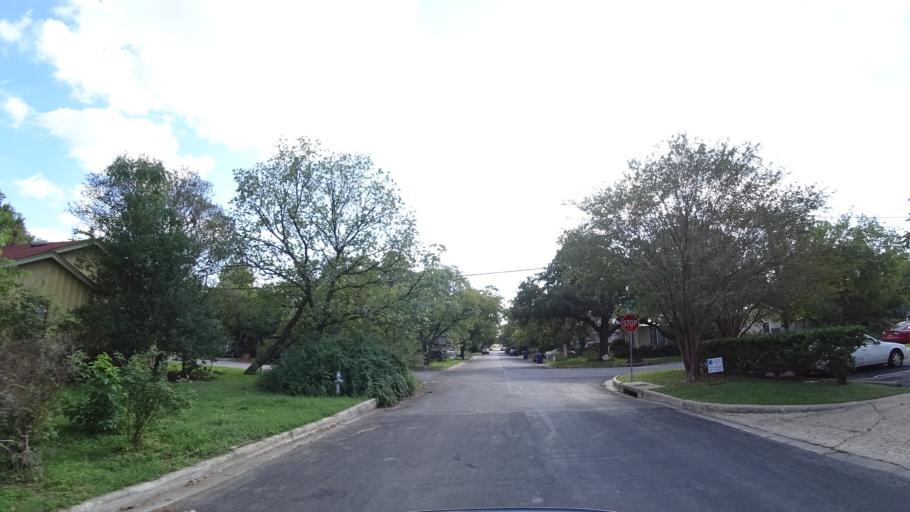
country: US
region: Texas
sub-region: Travis County
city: Austin
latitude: 30.3072
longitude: -97.7341
